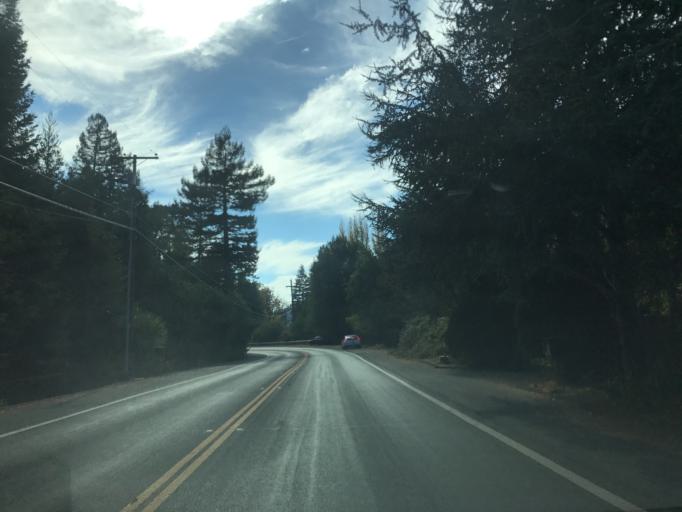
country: US
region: California
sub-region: Sonoma County
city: Guerneville
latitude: 38.5205
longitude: -122.9975
